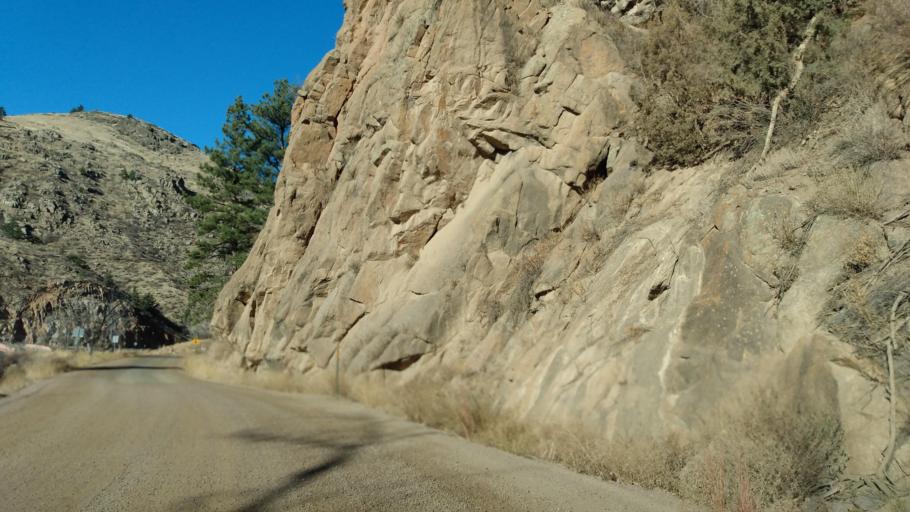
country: US
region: Colorado
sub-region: Boulder County
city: Lyons
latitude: 40.2413
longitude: -105.3121
